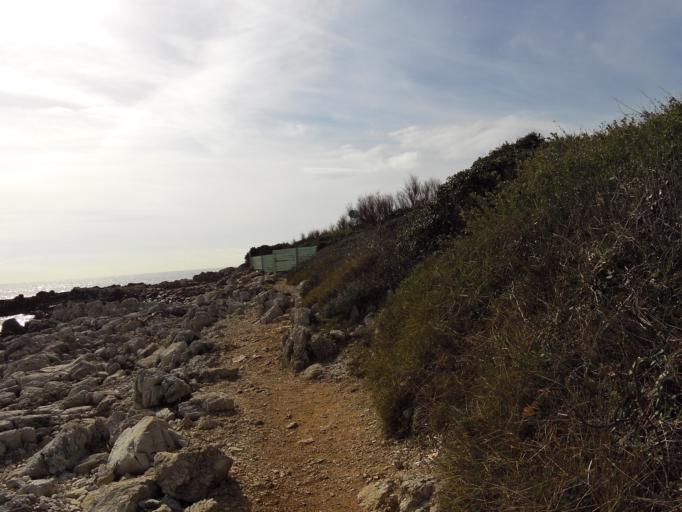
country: FR
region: Provence-Alpes-Cote d'Azur
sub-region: Departement des Alpes-Maritimes
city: Antibes
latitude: 43.5466
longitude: 7.1378
